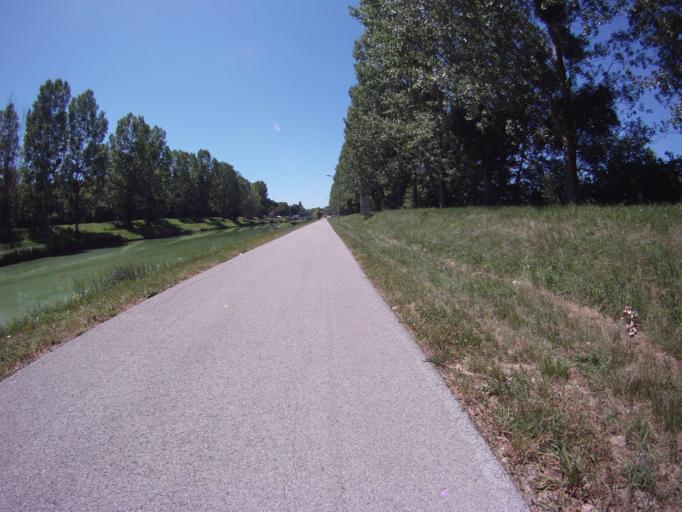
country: FR
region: Champagne-Ardenne
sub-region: Departement de la Marne
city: Mardeuil
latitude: 49.0665
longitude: 3.9088
